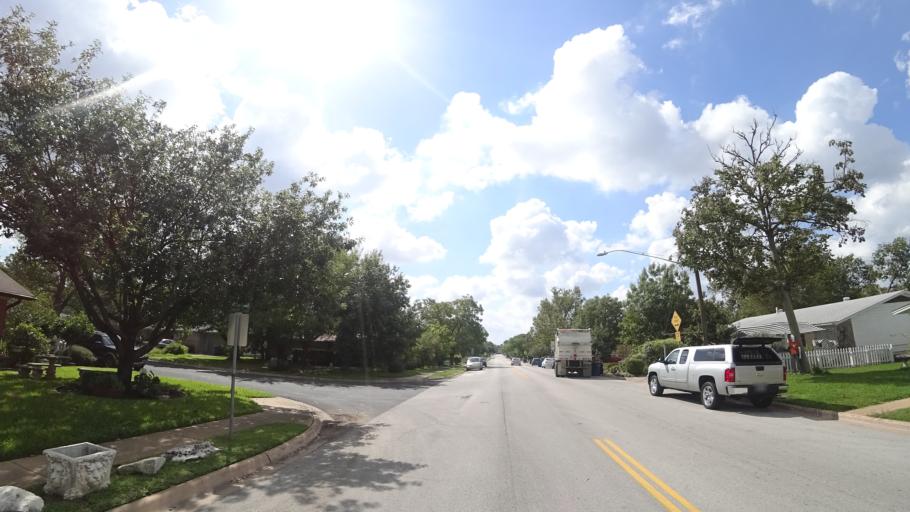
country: US
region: Texas
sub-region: Travis County
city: Austin
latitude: 30.3566
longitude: -97.7212
